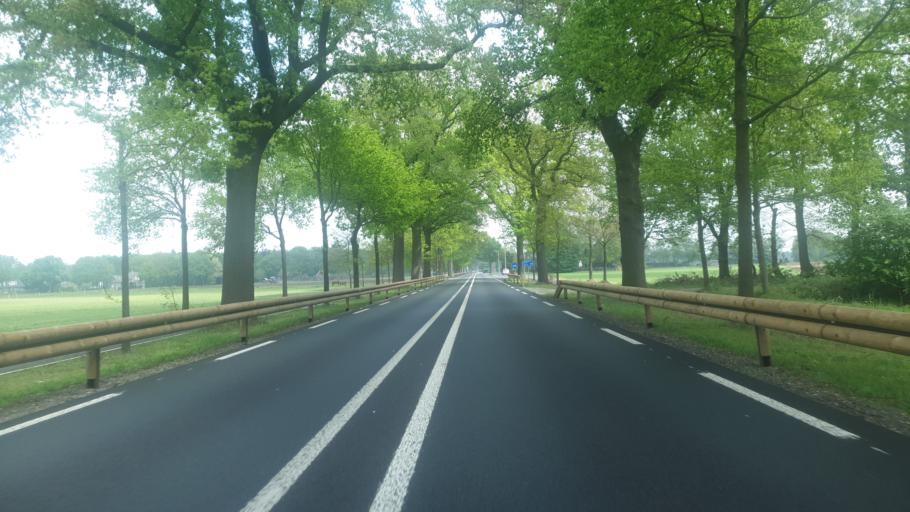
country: NL
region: North Brabant
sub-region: Gemeente Landerd
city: Reek
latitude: 51.7419
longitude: 5.6991
